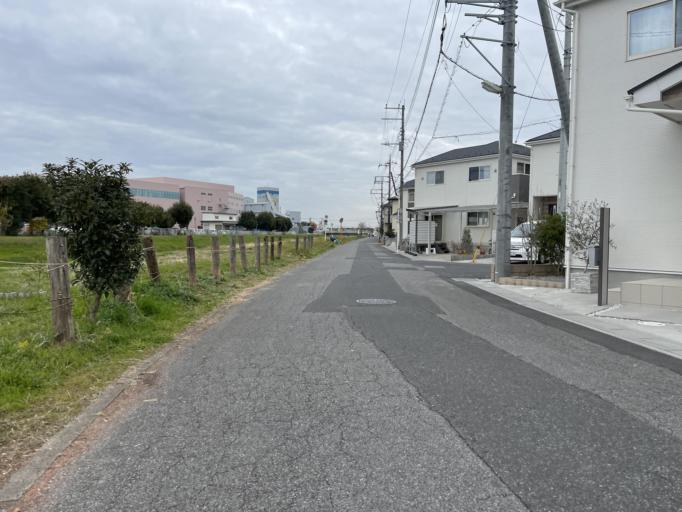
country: JP
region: Saitama
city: Shiraoka
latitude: 36.0269
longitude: 139.6495
